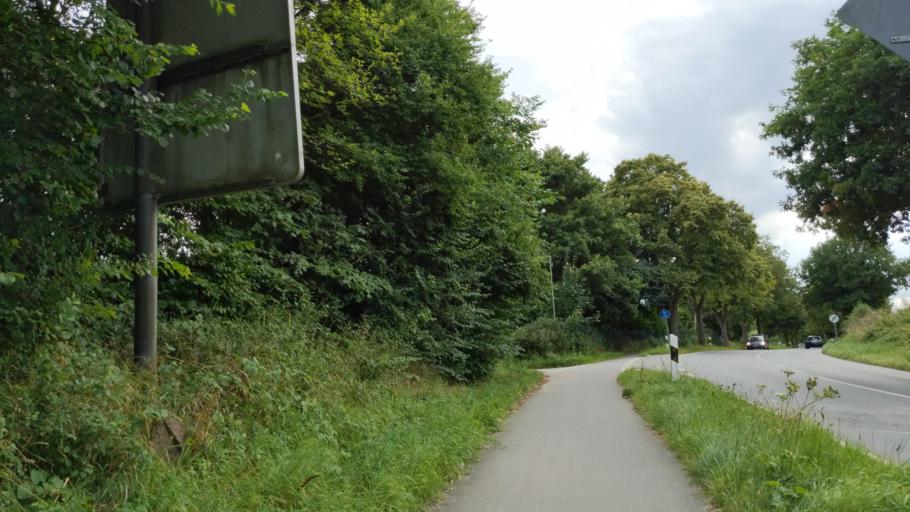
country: DE
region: Schleswig-Holstein
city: Altenkrempe
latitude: 54.1172
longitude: 10.8424
